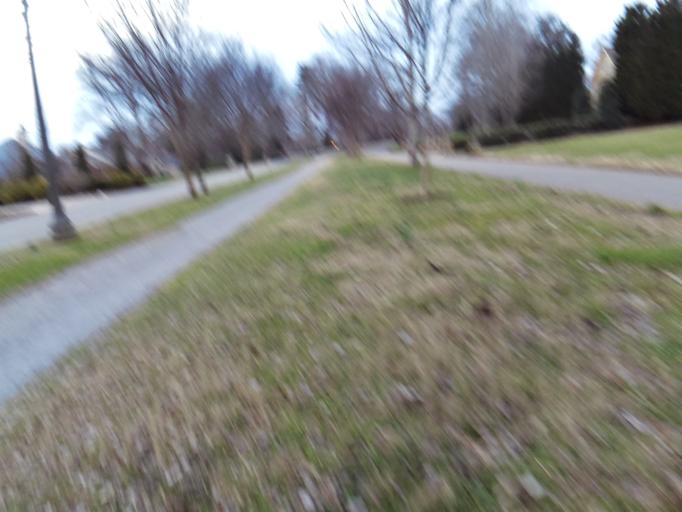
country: US
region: Tennessee
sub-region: Knox County
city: Knoxville
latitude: 35.9273
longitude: -83.9655
